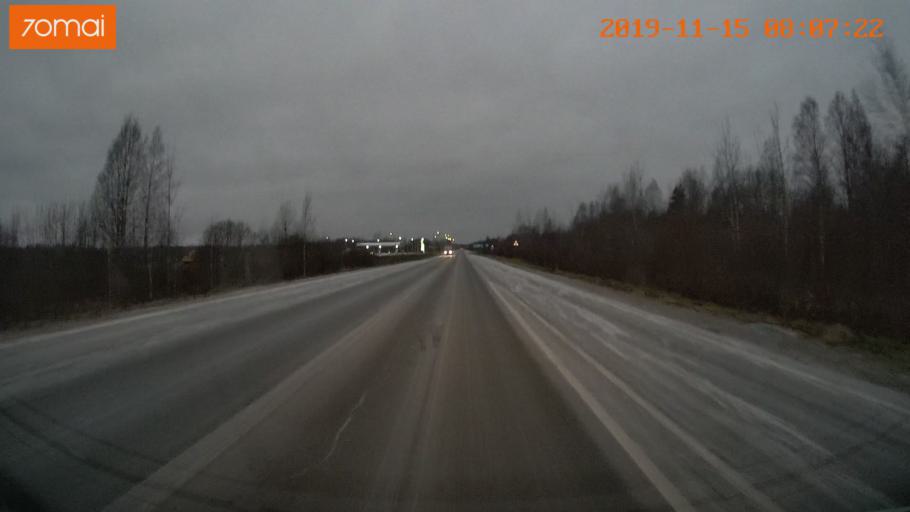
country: RU
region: Vologda
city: Cherepovets
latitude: 59.0263
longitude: 38.0173
